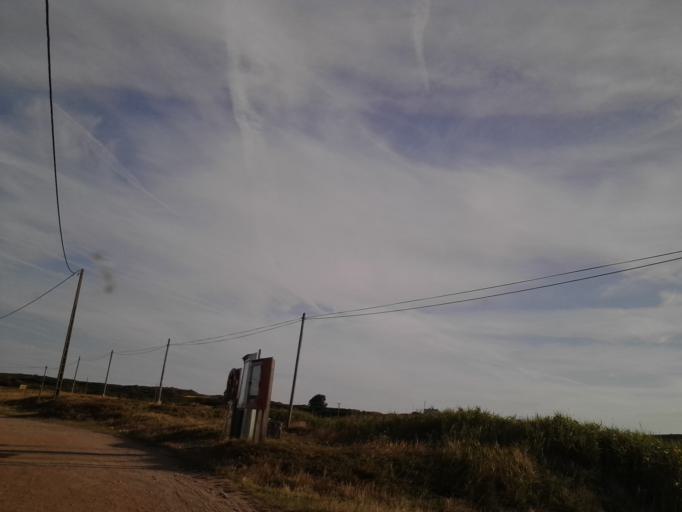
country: FR
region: Lower Normandy
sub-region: Departement de la Manche
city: Fermanville
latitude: 49.6873
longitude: -1.4722
